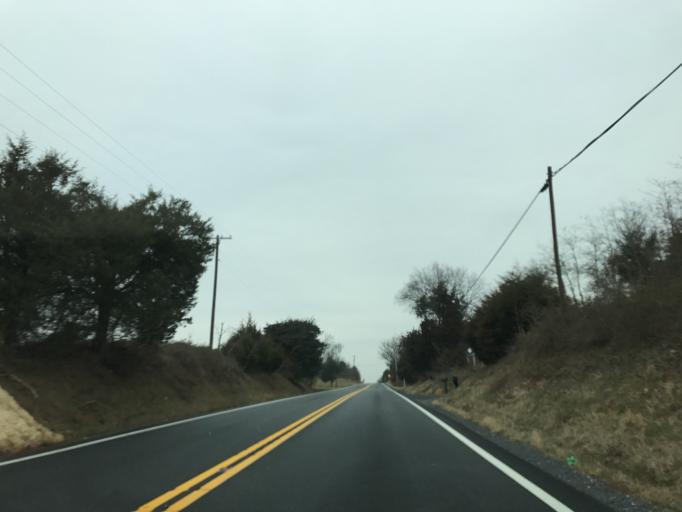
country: US
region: Maryland
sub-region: Frederick County
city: Emmitsburg
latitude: 39.6848
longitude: -77.2575
